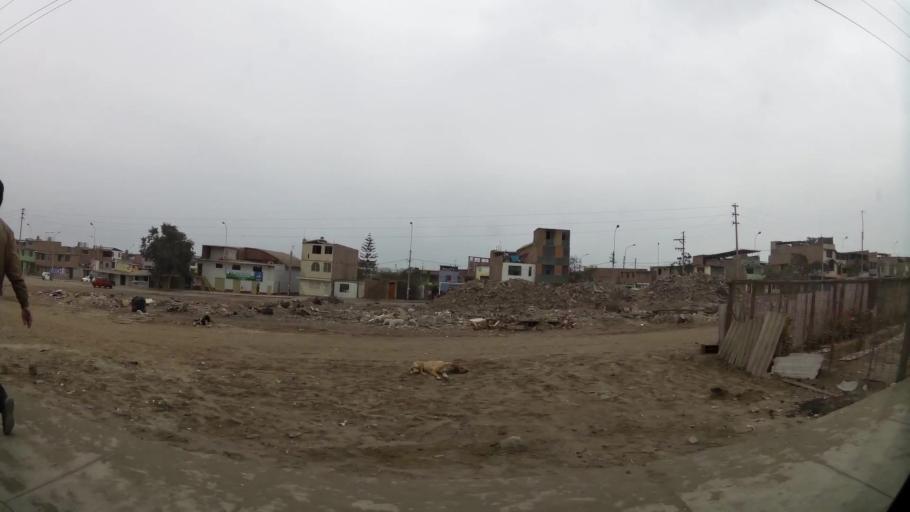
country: PE
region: Lima
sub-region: Lima
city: Surco
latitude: -12.2284
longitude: -76.9206
